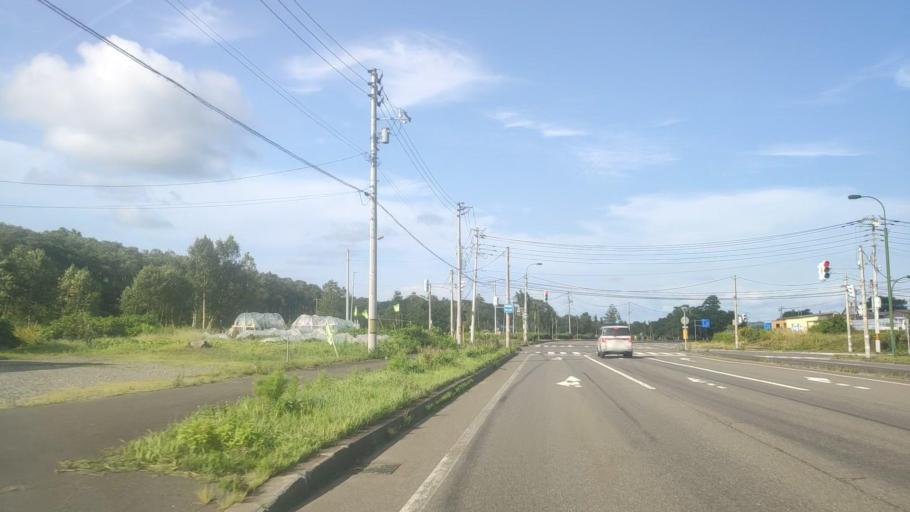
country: JP
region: Hokkaido
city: Chitose
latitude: 42.7681
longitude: 141.8182
